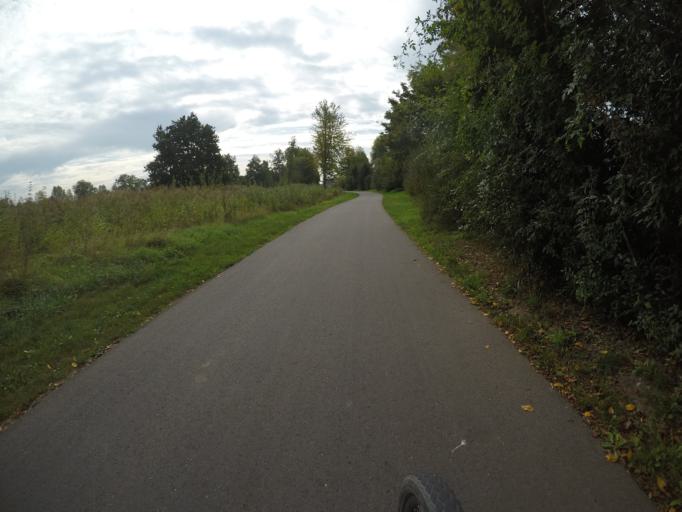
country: DE
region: Baden-Wuerttemberg
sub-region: Karlsruhe Region
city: Kronau
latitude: 49.2453
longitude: 8.6305
